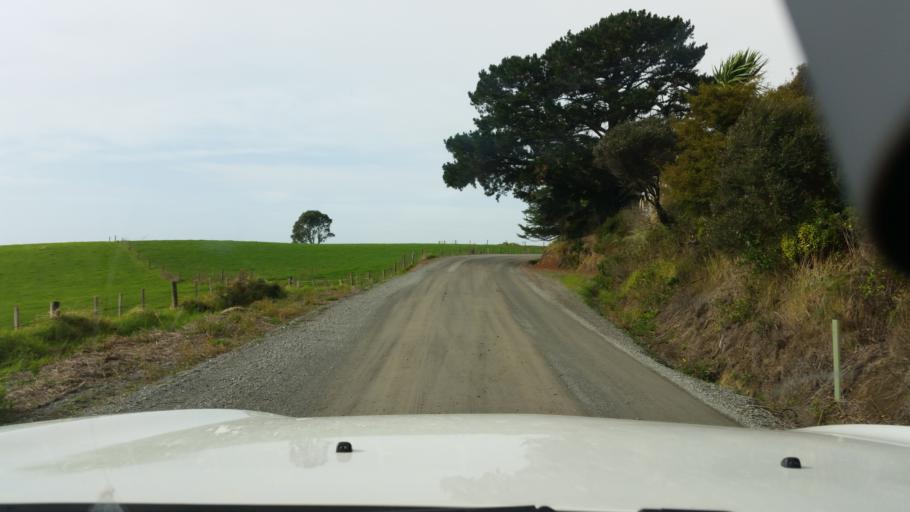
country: NZ
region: Northland
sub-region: Whangarei
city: Ruakaka
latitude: -35.8126
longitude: 174.5292
